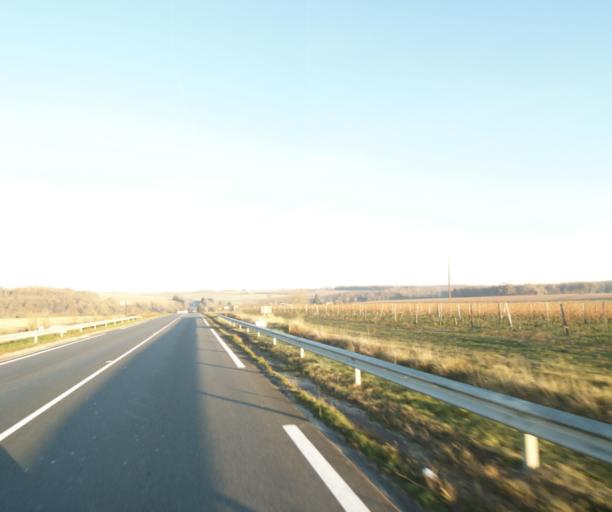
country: FR
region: Poitou-Charentes
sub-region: Departement de la Charente-Maritime
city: Cherac
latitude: 45.7138
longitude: -0.4928
